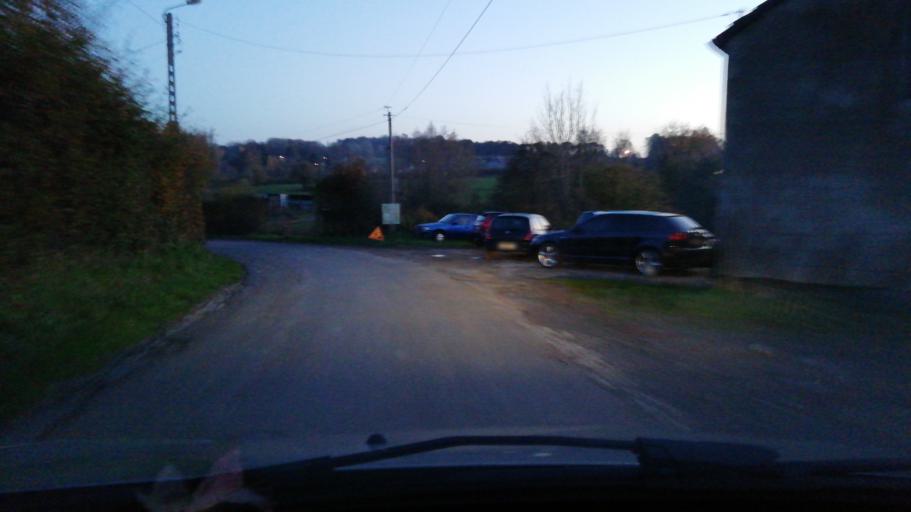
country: FR
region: Nord-Pas-de-Calais
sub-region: Departement du Nord
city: Marpent
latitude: 50.2568
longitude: 4.0880
